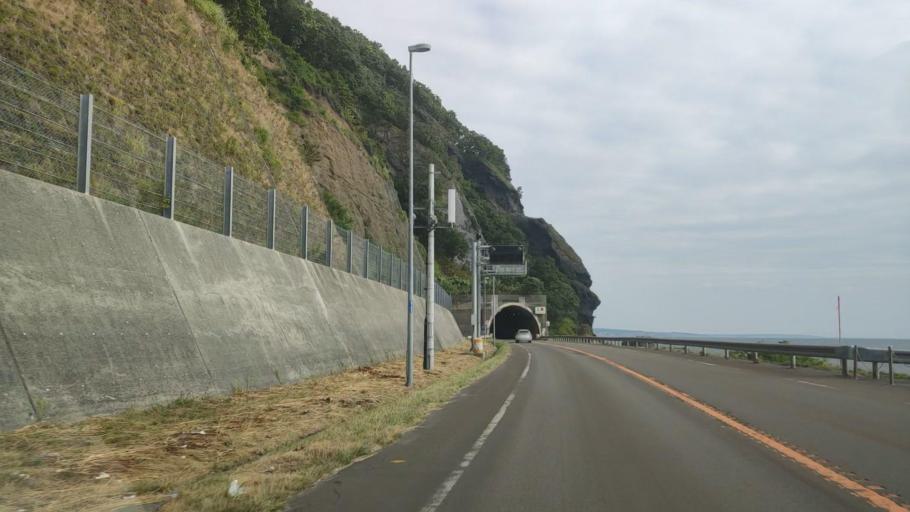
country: JP
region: Hokkaido
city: Ishikari
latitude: 43.4497
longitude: 141.4097
